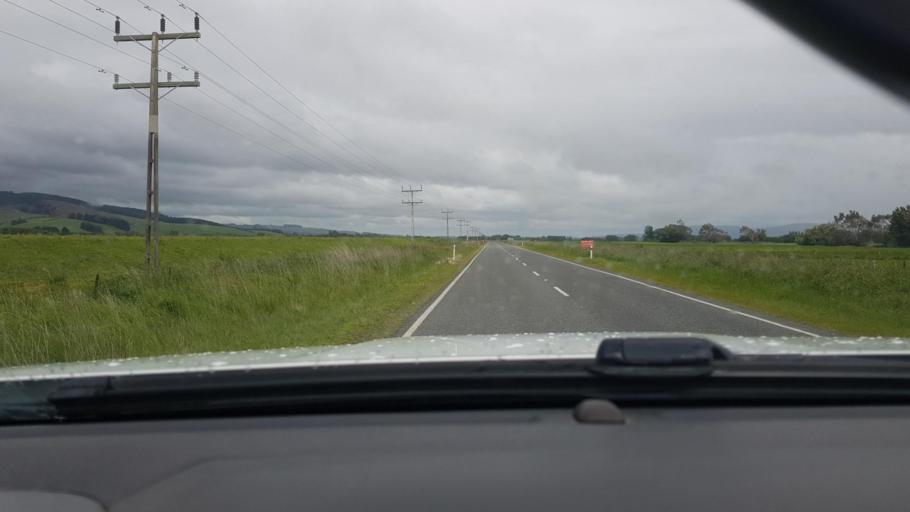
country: NZ
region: Southland
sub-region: Southland District
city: Winton
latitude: -45.8209
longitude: 168.3753
